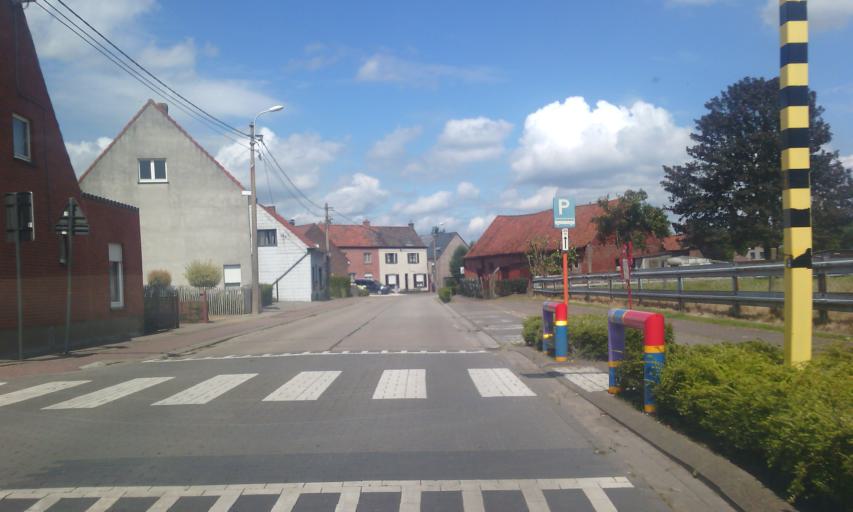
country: BE
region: Flanders
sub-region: Provincie Oost-Vlaanderen
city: Lochristi
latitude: 51.1037
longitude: 3.8985
